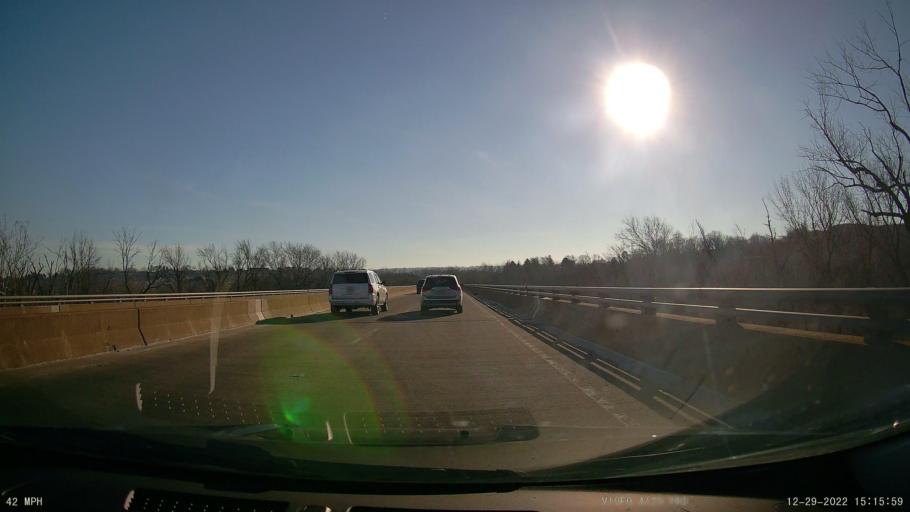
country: US
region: Pennsylvania
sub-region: Montgomery County
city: Bridgeport
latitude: 40.1113
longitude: -75.3506
